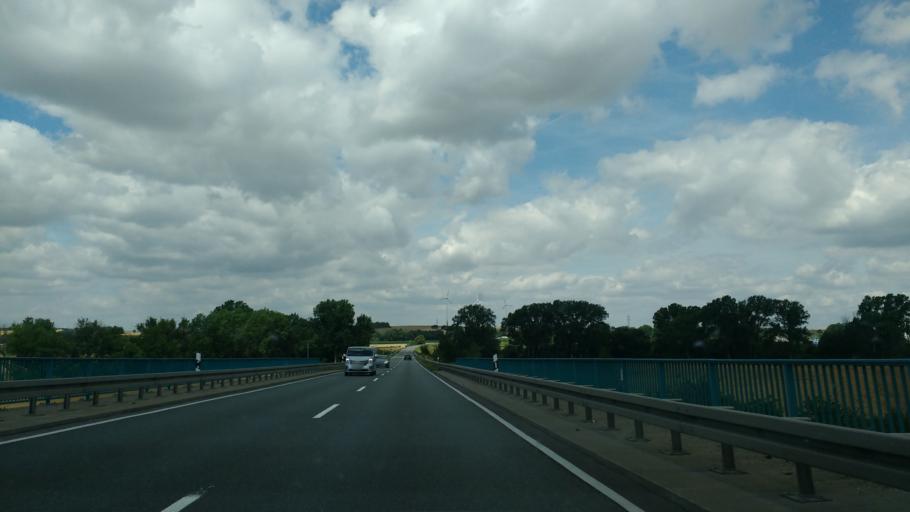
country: DE
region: Saxony-Anhalt
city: Zeitz
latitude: 51.0388
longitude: 12.1125
